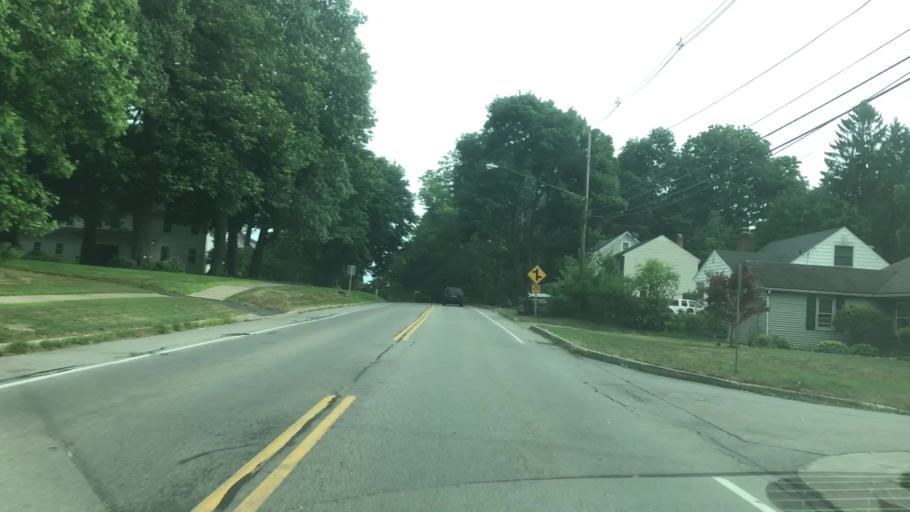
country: US
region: New York
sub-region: Monroe County
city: East Rochester
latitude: 43.1248
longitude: -77.4760
